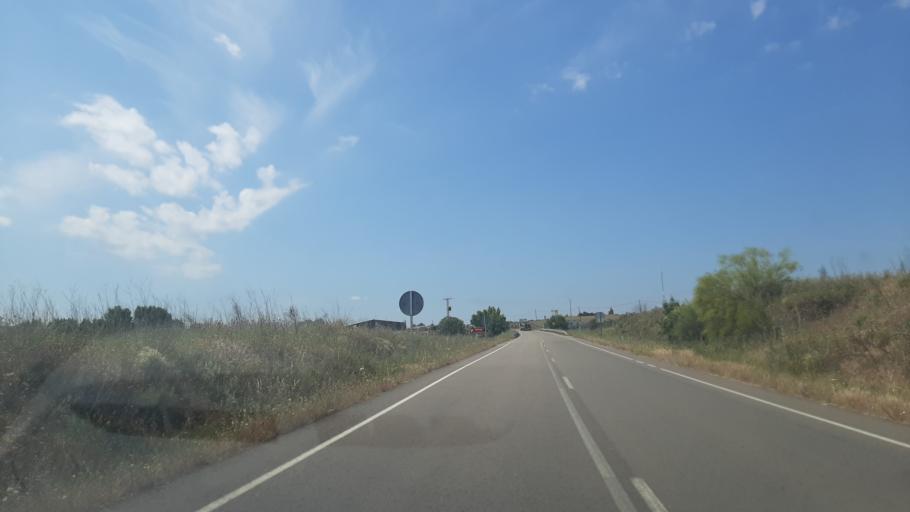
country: ES
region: Castille and Leon
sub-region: Provincia de Salamanca
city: Gallegos de Arganan
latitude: 40.6238
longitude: -6.7041
